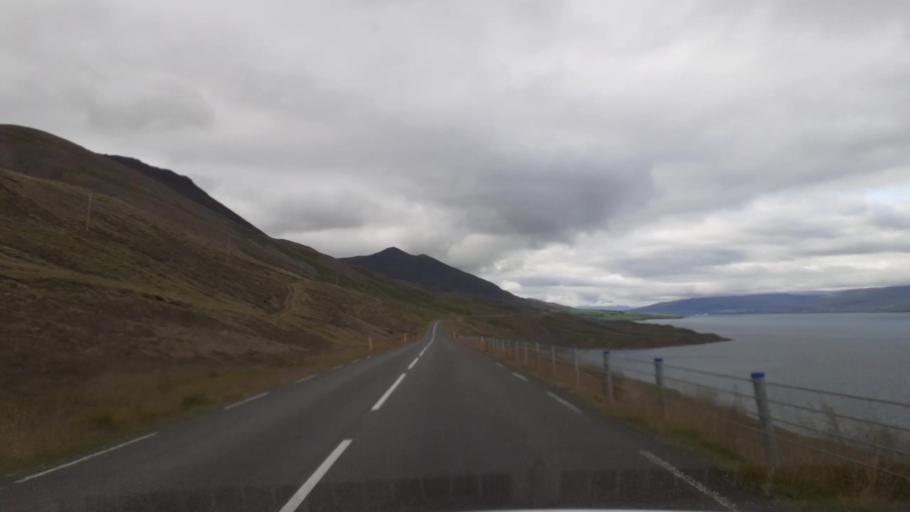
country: IS
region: Northeast
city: Akureyri
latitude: 65.8472
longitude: -18.0590
